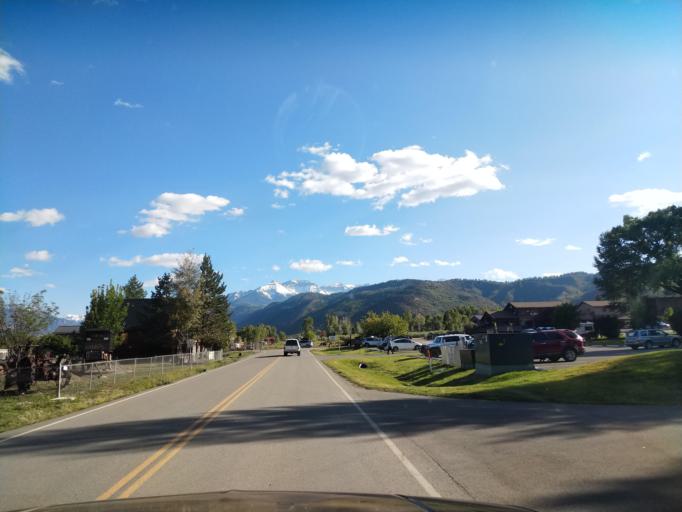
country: US
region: Colorado
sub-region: Ouray County
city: Ouray
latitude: 38.1524
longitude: -107.7550
